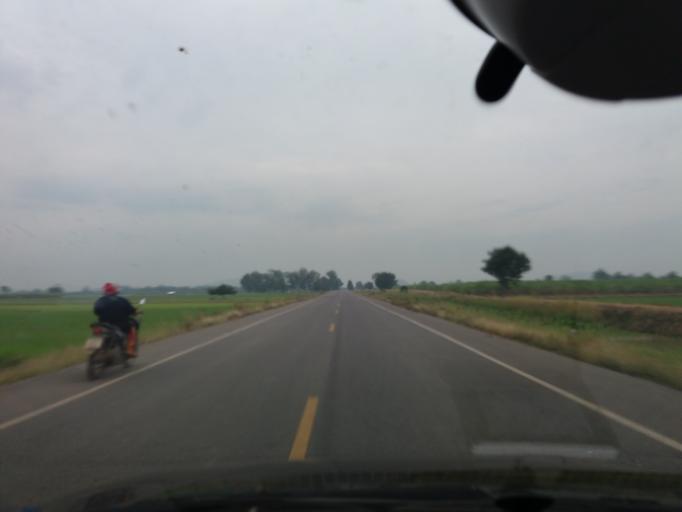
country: TH
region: Suphan Buri
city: Doem Bang Nang Buat
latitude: 14.8689
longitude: 100.1320
